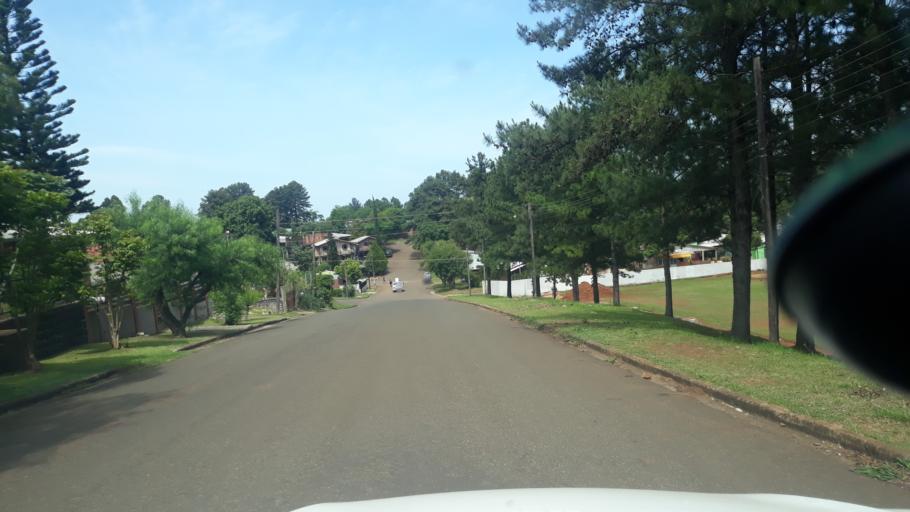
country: AR
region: Misiones
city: Bernardo de Irigoyen
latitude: -26.2520
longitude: -53.6480
